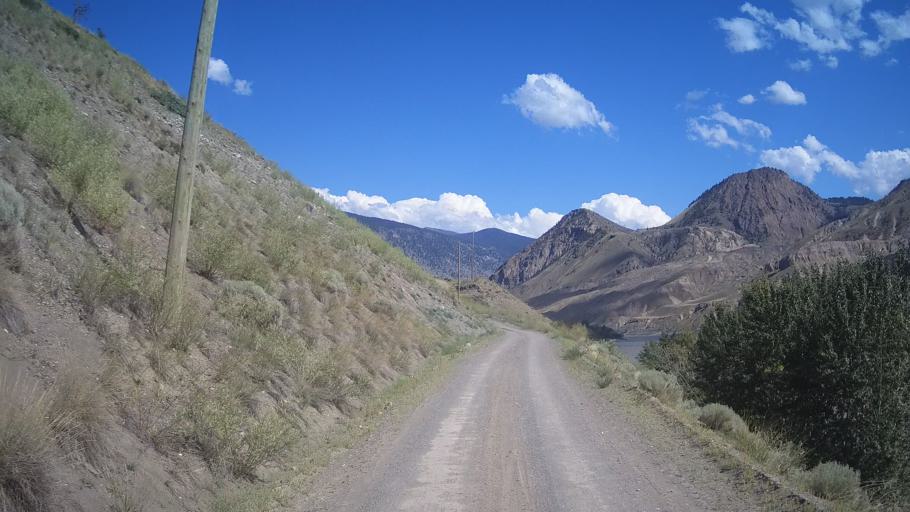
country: CA
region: British Columbia
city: Lillooet
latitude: 51.1821
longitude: -122.1279
